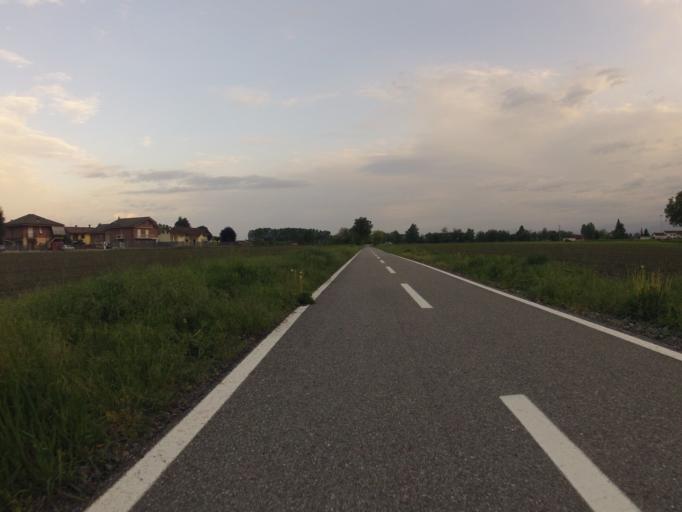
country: IT
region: Piedmont
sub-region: Provincia di Torino
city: Vigone
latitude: 44.8364
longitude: 7.4917
